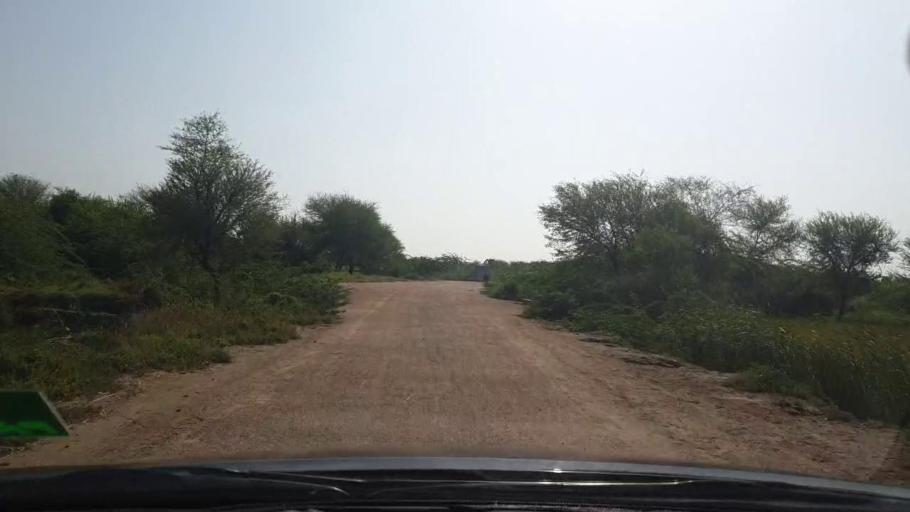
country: PK
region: Sindh
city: Tando Bago
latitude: 24.6970
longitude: 69.0196
